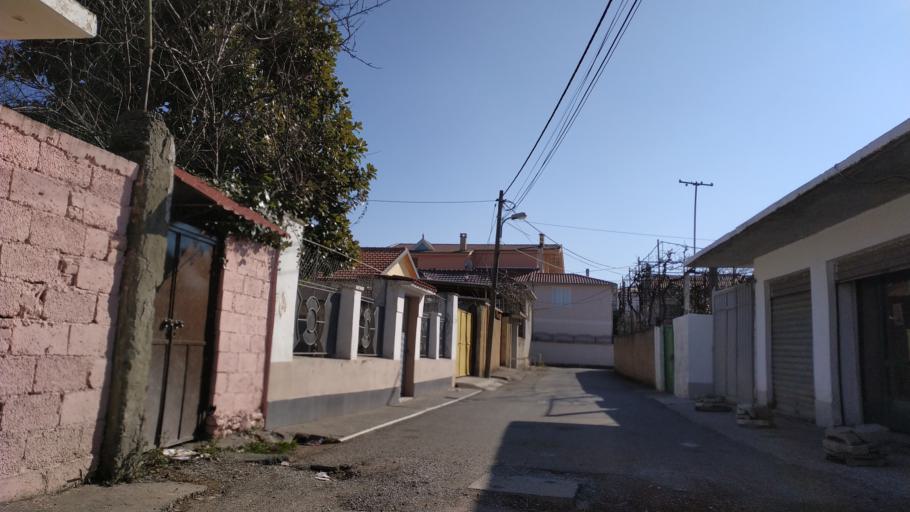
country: AL
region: Shkoder
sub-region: Rrethi i Shkodres
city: Shkoder
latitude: 42.0656
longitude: 19.5218
